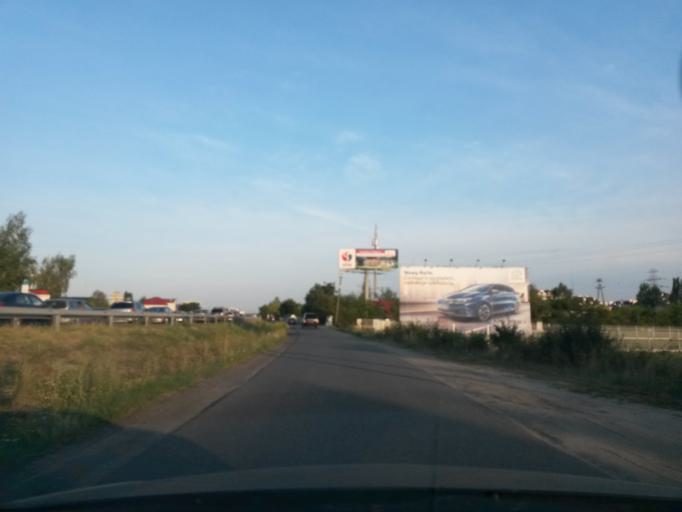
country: PL
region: Masovian Voivodeship
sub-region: Powiat warszawski zachodni
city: Kielpin
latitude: 52.3407
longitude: 20.8674
